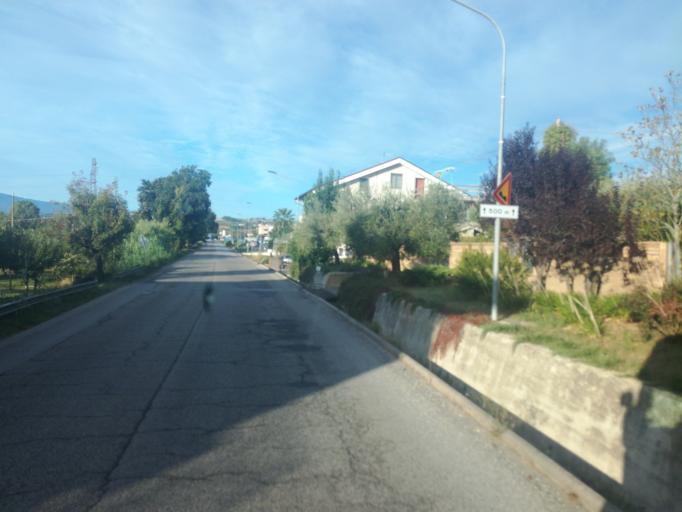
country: IT
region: Abruzzo
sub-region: Provincia di Chieti
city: Miglianico
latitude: 42.3681
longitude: 14.2879
